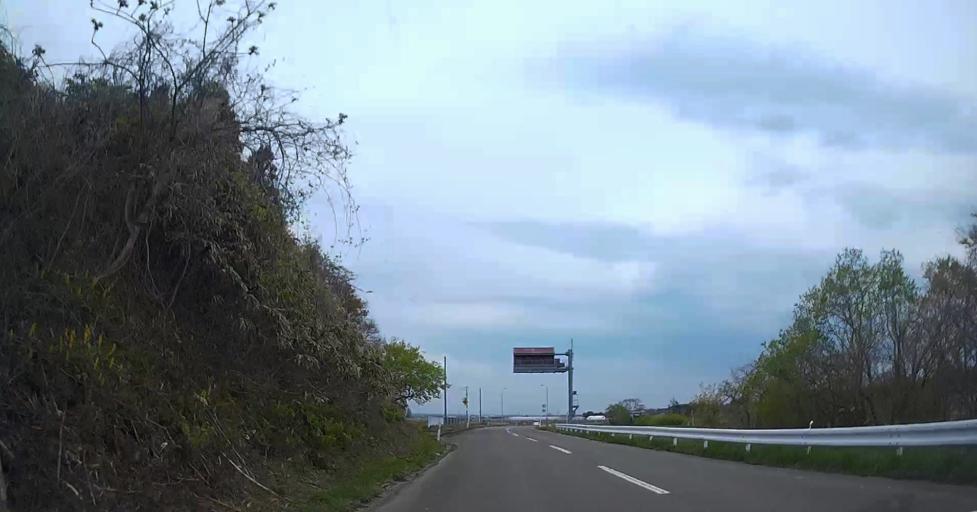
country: JP
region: Aomori
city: Goshogawara
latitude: 40.8984
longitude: 140.4861
